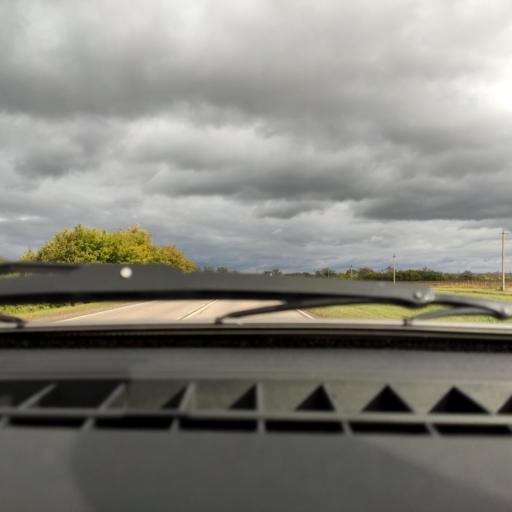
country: RU
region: Bashkortostan
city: Rayevskiy
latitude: 54.0135
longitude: 54.8684
